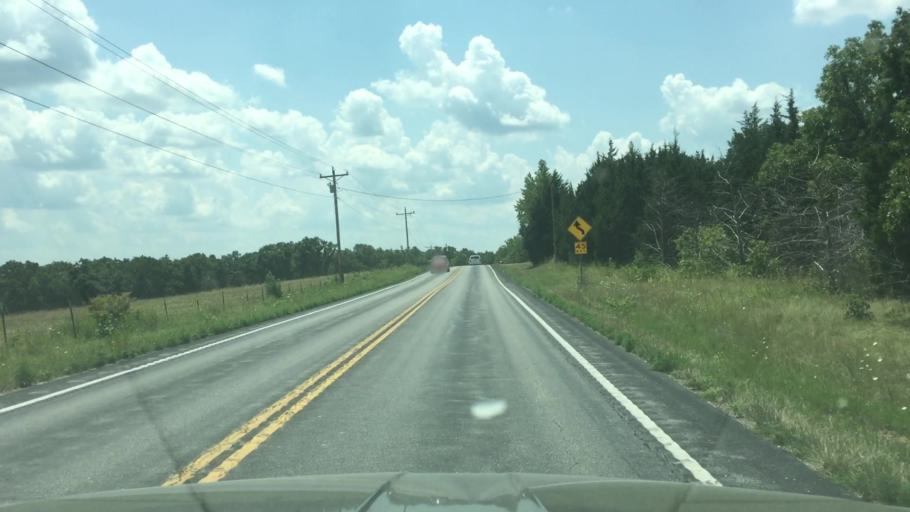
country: US
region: Missouri
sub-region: Miller County
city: Tuscumbia
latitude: 38.1096
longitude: -92.5028
